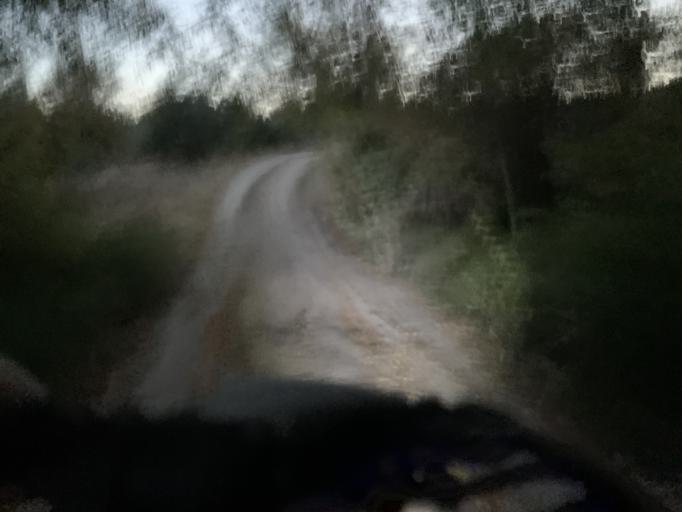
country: ES
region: Andalusia
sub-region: Provincia de Granada
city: Beas de Granada
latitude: 37.2198
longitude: -3.4543
